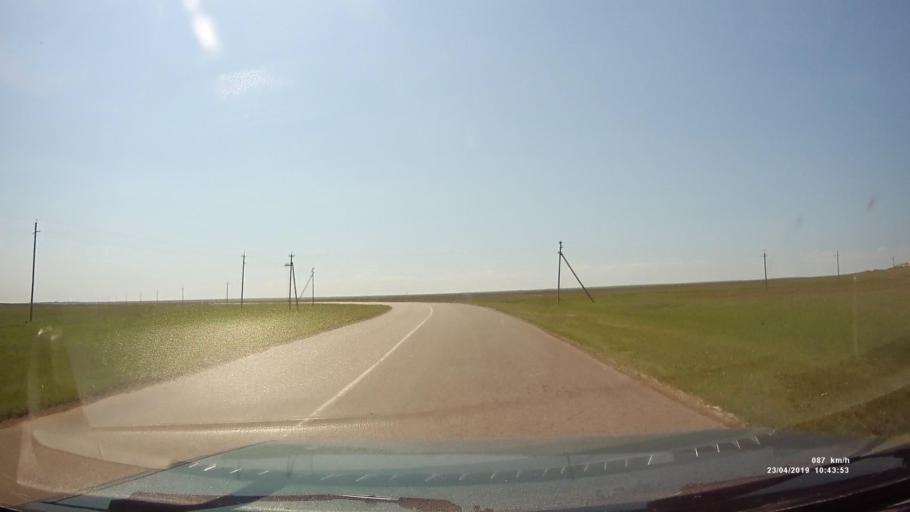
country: RU
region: Kalmykiya
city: Yashalta
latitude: 46.4647
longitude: 42.6502
